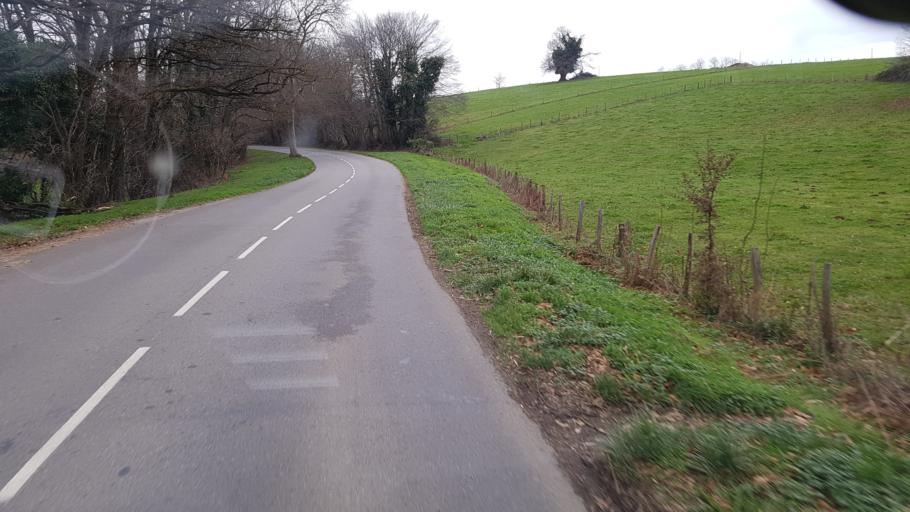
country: FR
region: Limousin
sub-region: Departement de la Correze
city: Donzenac
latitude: 45.2455
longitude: 1.5341
